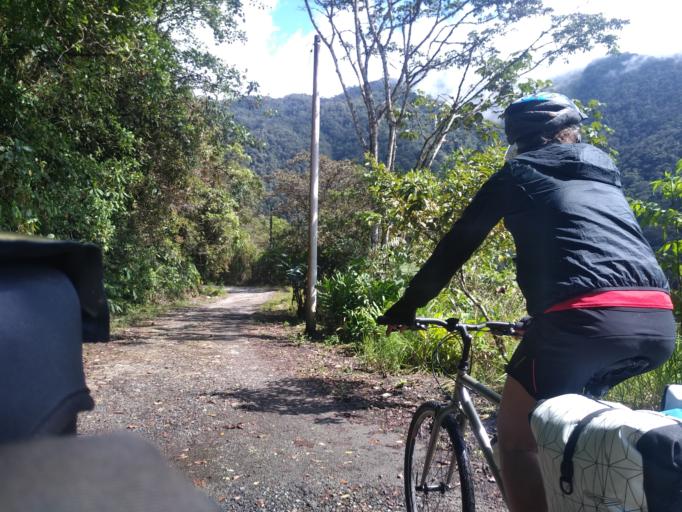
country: EC
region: Tungurahua
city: Banos
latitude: -1.4029
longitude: -78.2806
